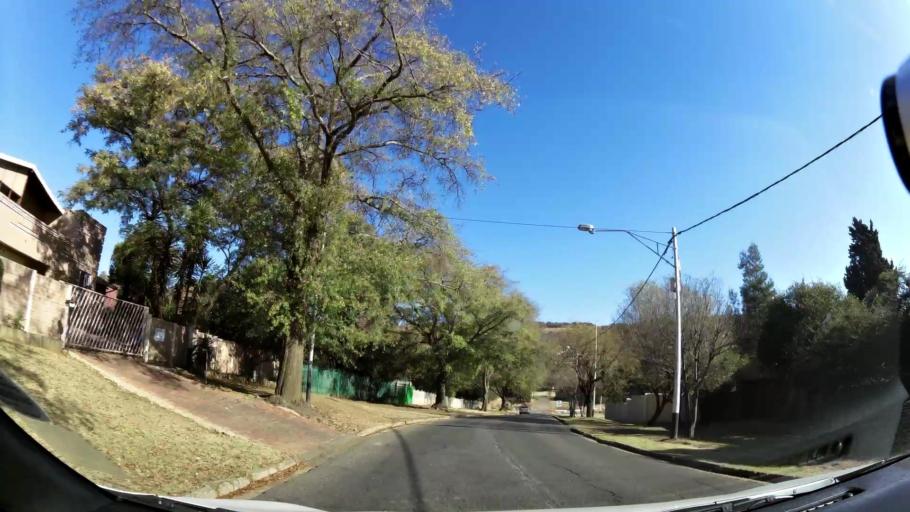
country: ZA
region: Gauteng
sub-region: City of Johannesburg Metropolitan Municipality
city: Johannesburg
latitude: -26.2805
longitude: 28.0093
